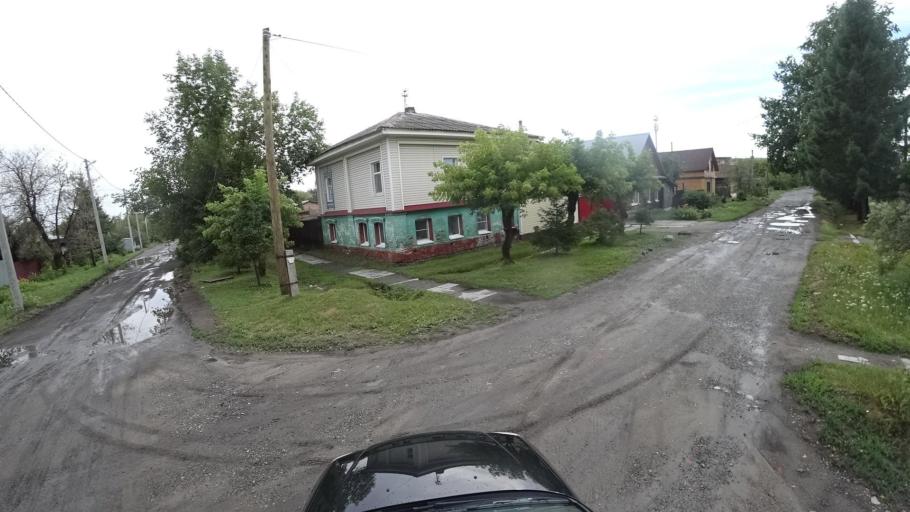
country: RU
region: Sverdlovsk
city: Kamyshlov
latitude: 56.8440
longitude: 62.7231
